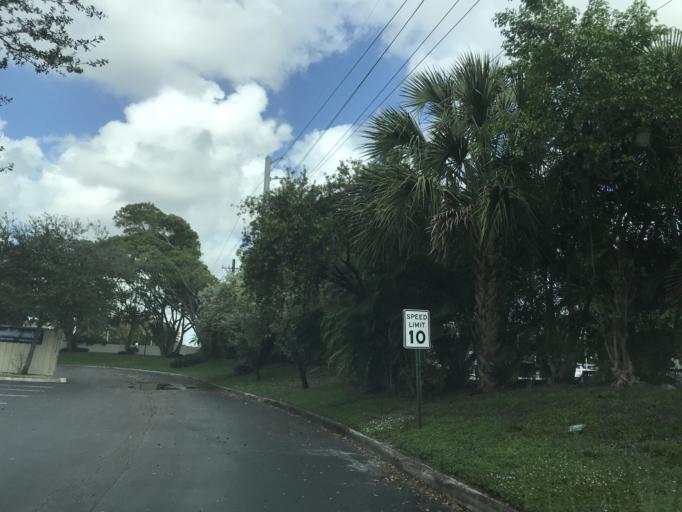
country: US
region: Florida
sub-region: Broward County
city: Coconut Creek
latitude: 26.2729
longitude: -80.1867
